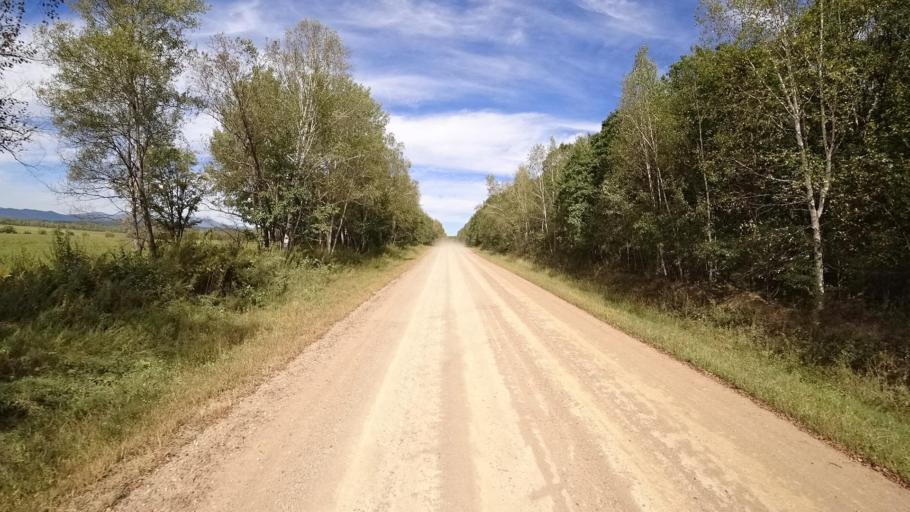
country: RU
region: Primorskiy
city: Yakovlevka
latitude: 44.6249
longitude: 133.5996
